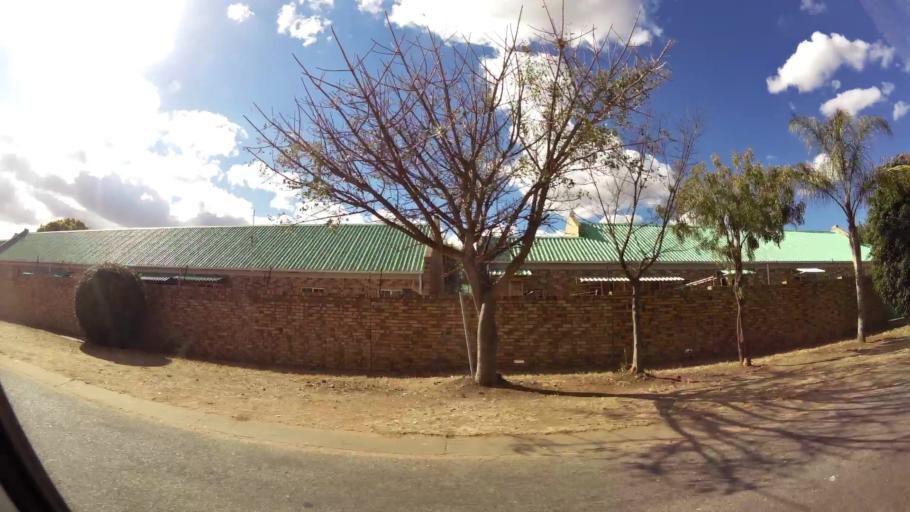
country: ZA
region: Limpopo
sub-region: Capricorn District Municipality
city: Polokwane
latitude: -23.8881
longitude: 29.4695
